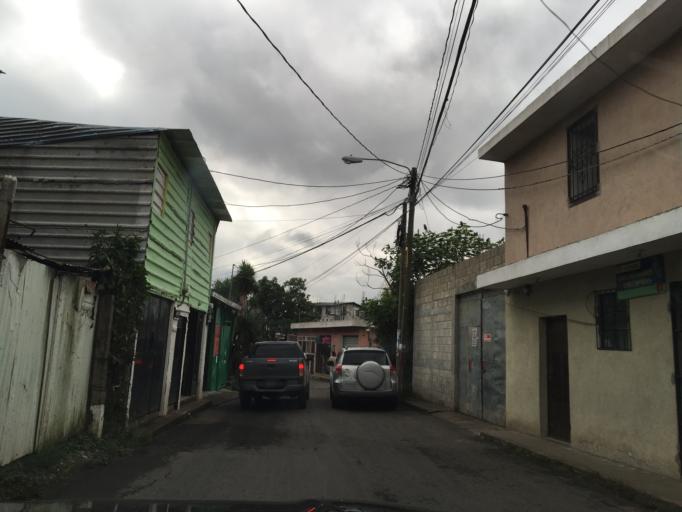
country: GT
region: Guatemala
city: Mixco
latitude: 14.6212
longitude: -90.5859
